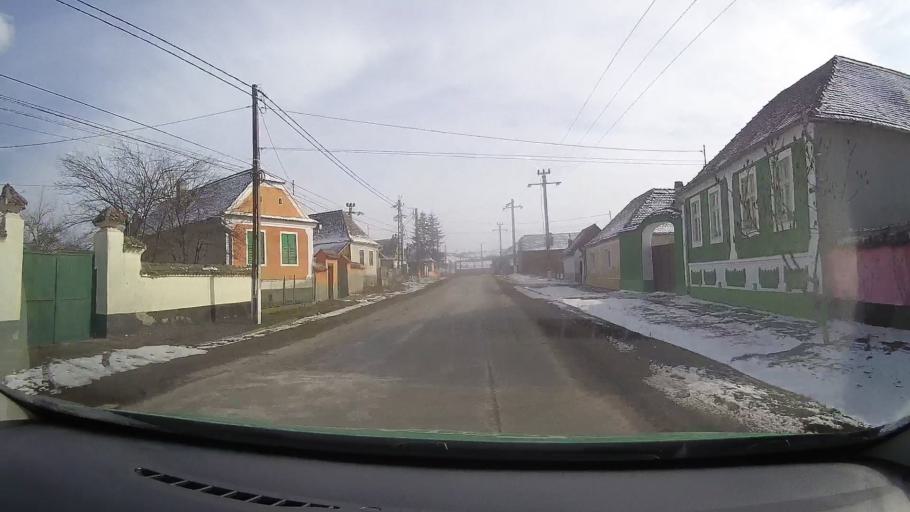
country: RO
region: Mures
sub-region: Comuna Apold
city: Apold
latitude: 46.1231
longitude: 24.8190
